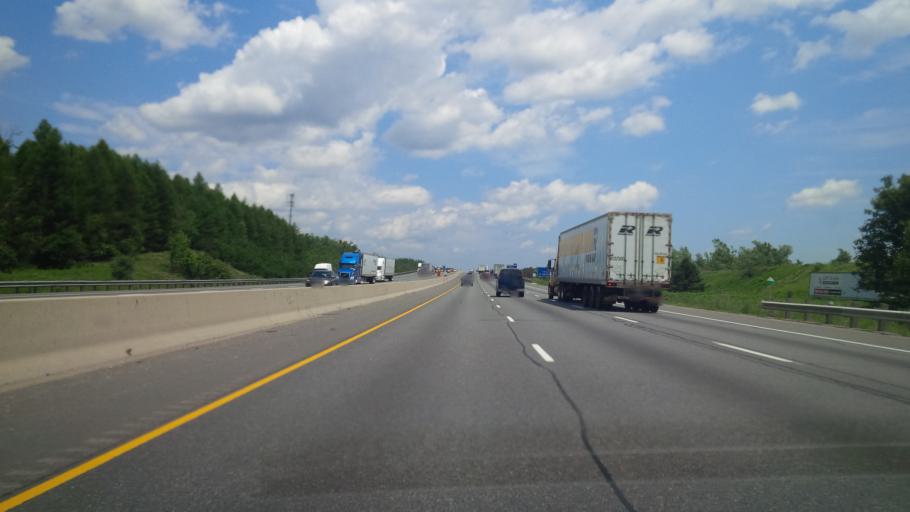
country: CA
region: Ontario
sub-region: Halton
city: Milton
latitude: 43.4781
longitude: -80.0185
